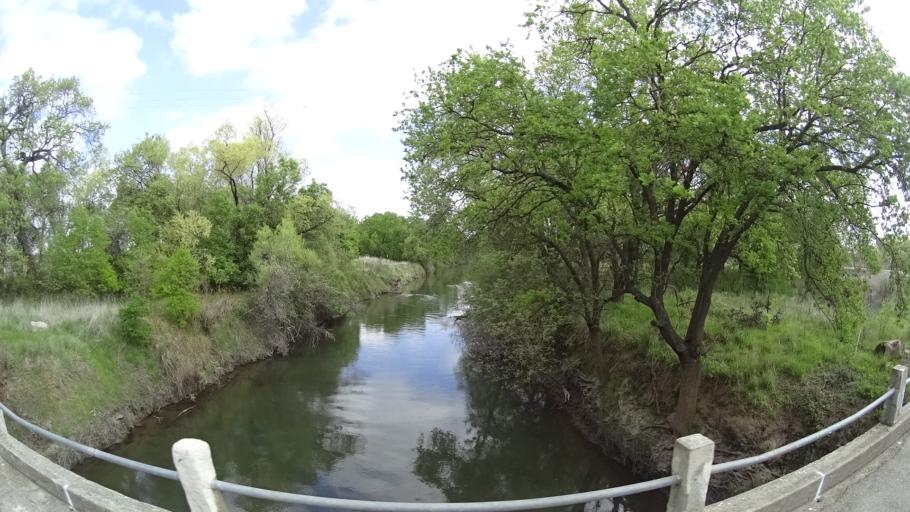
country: US
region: California
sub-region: Butte County
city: Biggs
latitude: 39.4198
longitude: -121.8812
